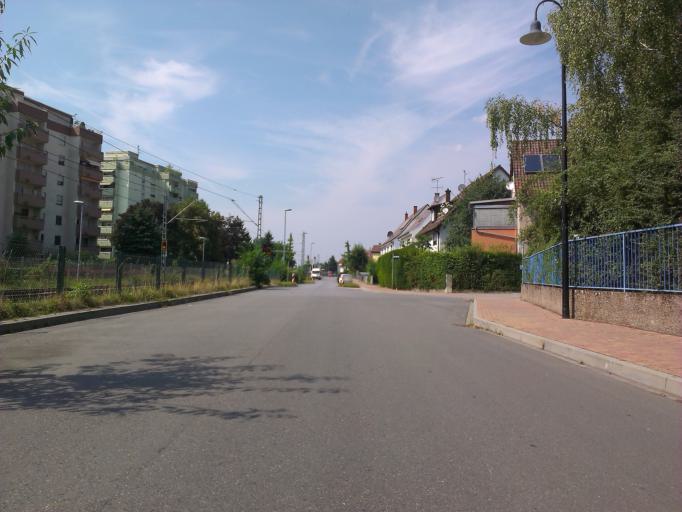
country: DE
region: Baden-Wuerttemberg
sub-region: Karlsruhe Region
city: Edingen-Neckarhausen
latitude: 49.4460
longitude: 8.6061
